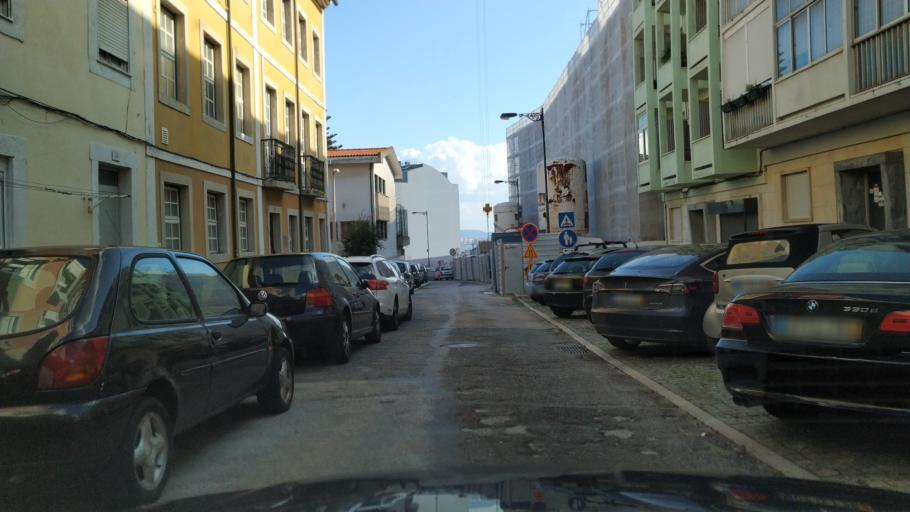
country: PT
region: Lisbon
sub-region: Lisbon
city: Lisbon
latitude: 38.7192
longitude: -9.1262
